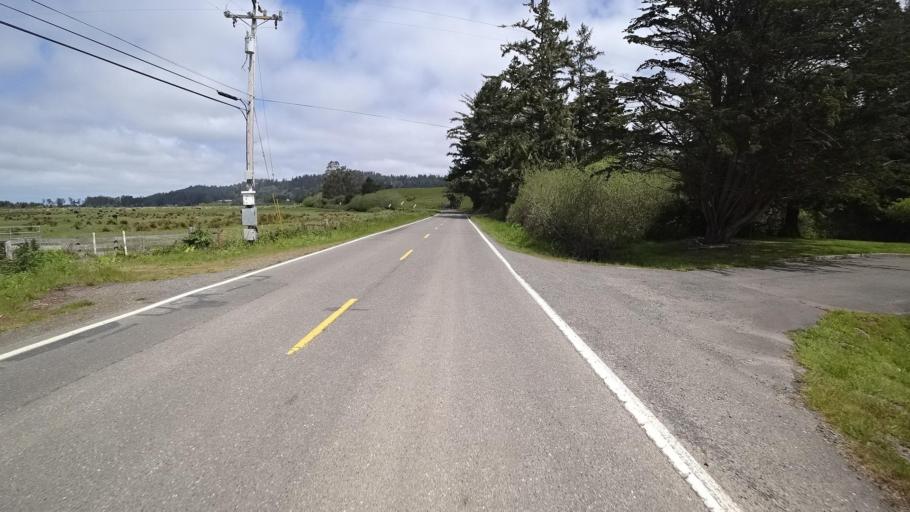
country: US
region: California
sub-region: Humboldt County
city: Humboldt Hill
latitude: 40.6864
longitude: -124.1975
